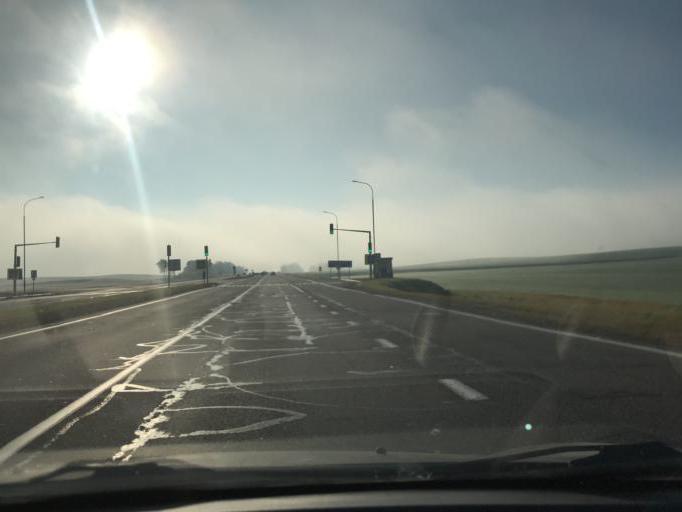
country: BY
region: Minsk
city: Luhavaya Slabada
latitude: 53.7362
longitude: 27.8469
